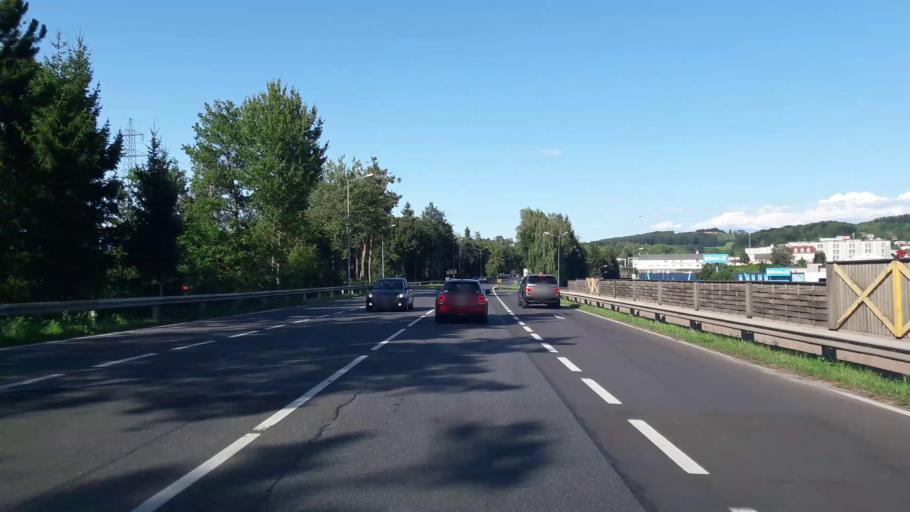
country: AT
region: Styria
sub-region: Politischer Bezirk Weiz
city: Gleisdorf
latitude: 47.1084
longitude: 15.6992
